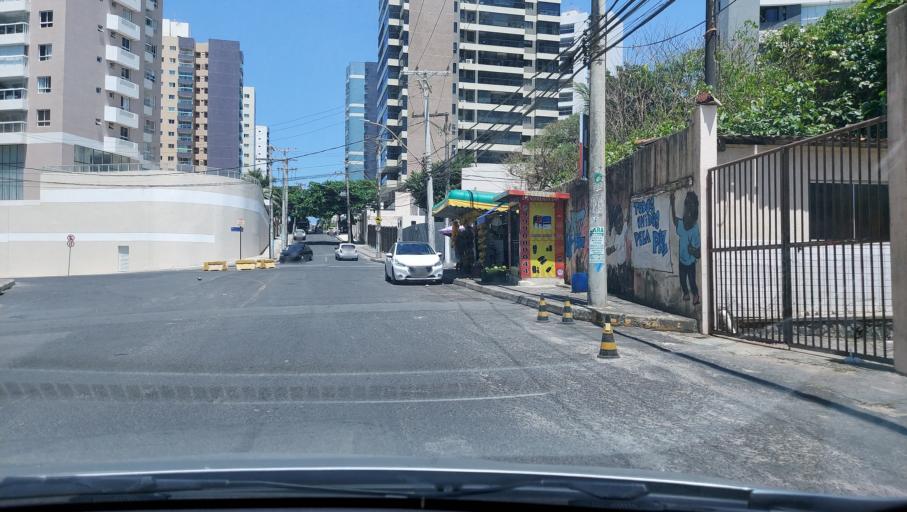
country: BR
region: Bahia
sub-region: Salvador
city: Salvador
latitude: -12.9863
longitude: -38.4379
